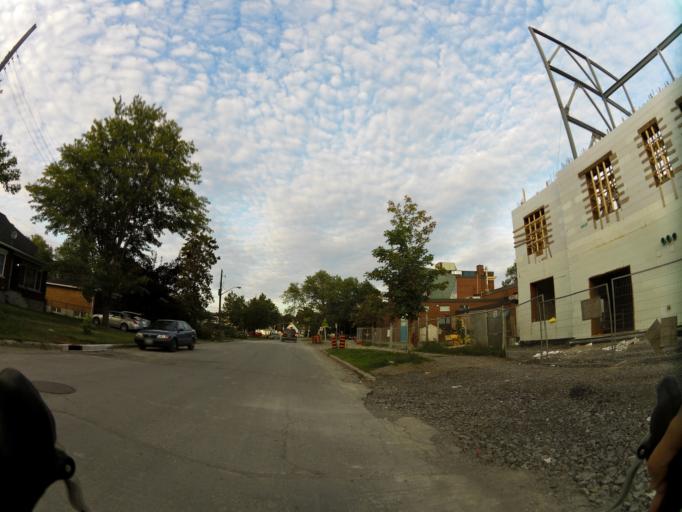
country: CA
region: Ontario
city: Ottawa
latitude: 45.3833
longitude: -75.7342
